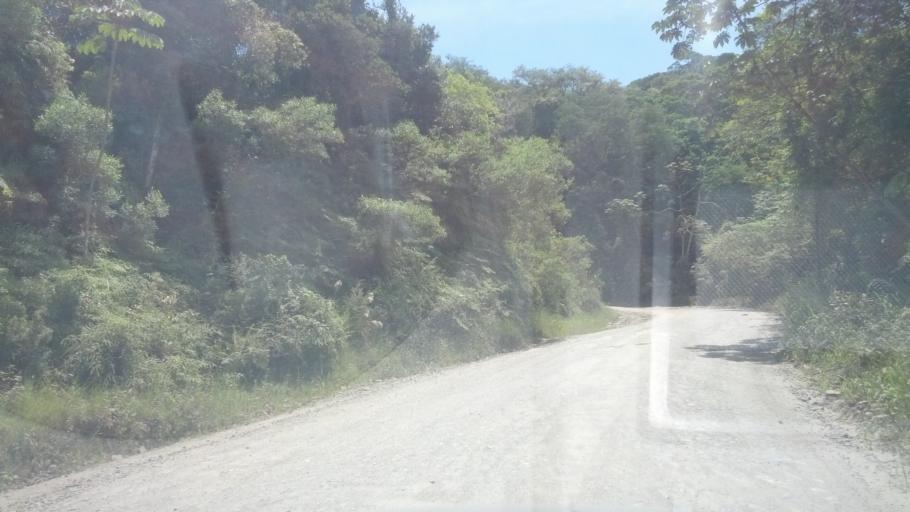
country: BR
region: Santa Catarina
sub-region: Porto Belo
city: Porto Belo
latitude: -27.1648
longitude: -48.5283
